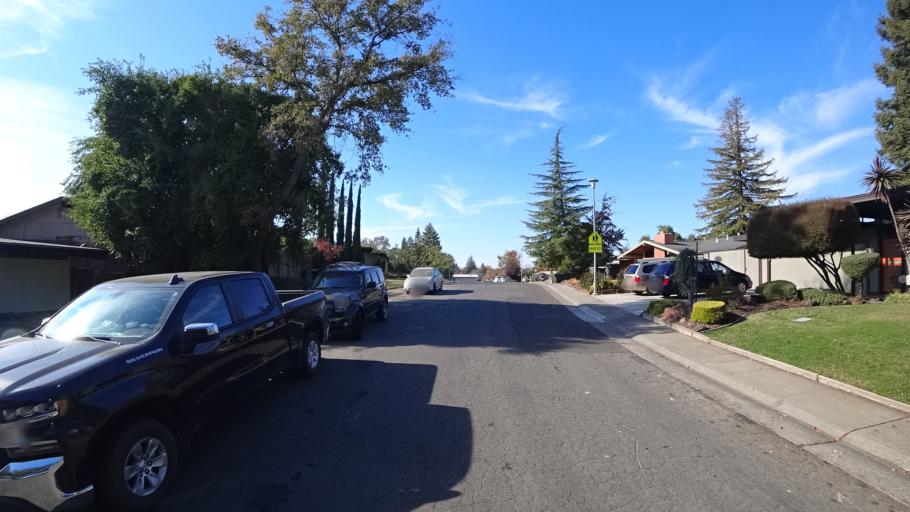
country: US
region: California
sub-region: Sacramento County
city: Fair Oaks
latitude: 38.6681
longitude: -121.2832
